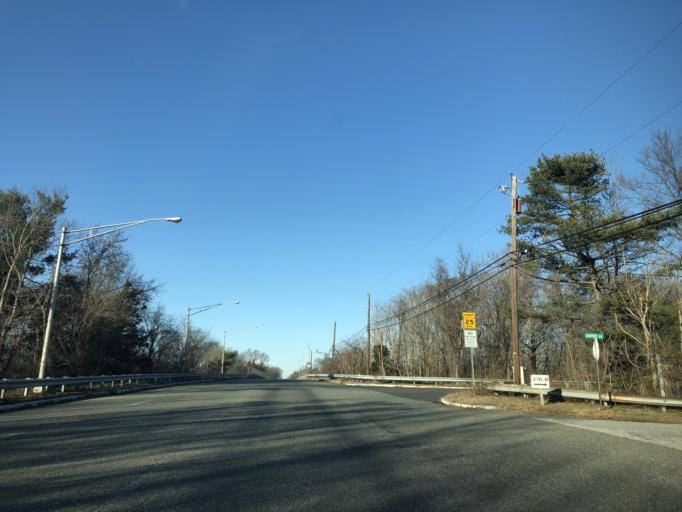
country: US
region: New Jersey
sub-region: Gloucester County
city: Beckett
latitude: 39.7310
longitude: -75.4059
